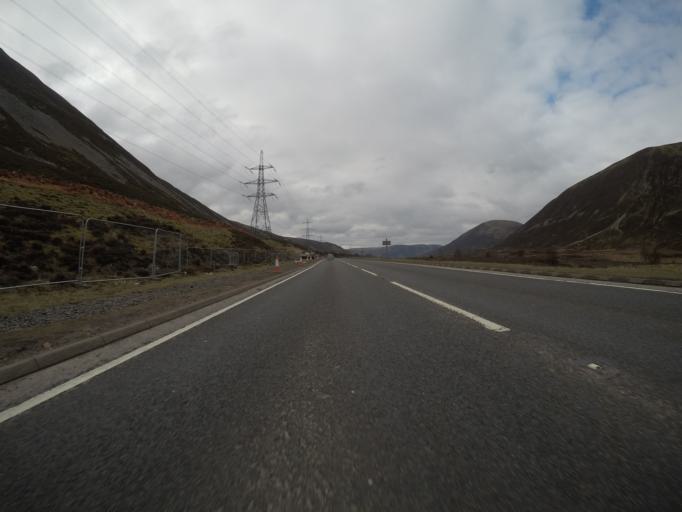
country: GB
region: Scotland
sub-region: Highland
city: Kingussie
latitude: 56.8657
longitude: -4.2539
